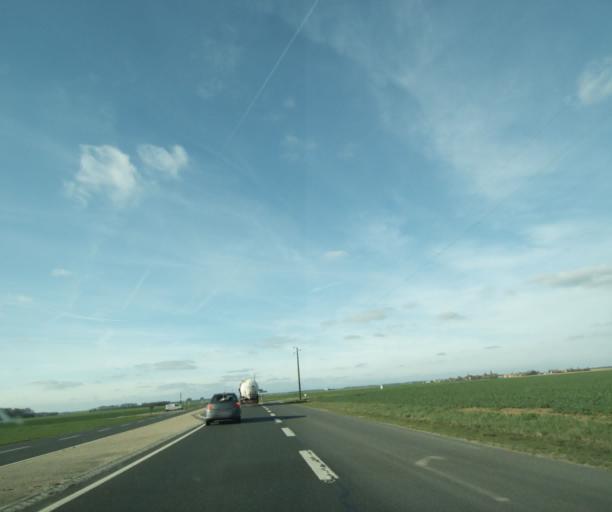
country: FR
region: Ile-de-France
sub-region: Departement des Yvelines
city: Ablis
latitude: 48.4827
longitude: 1.8491
